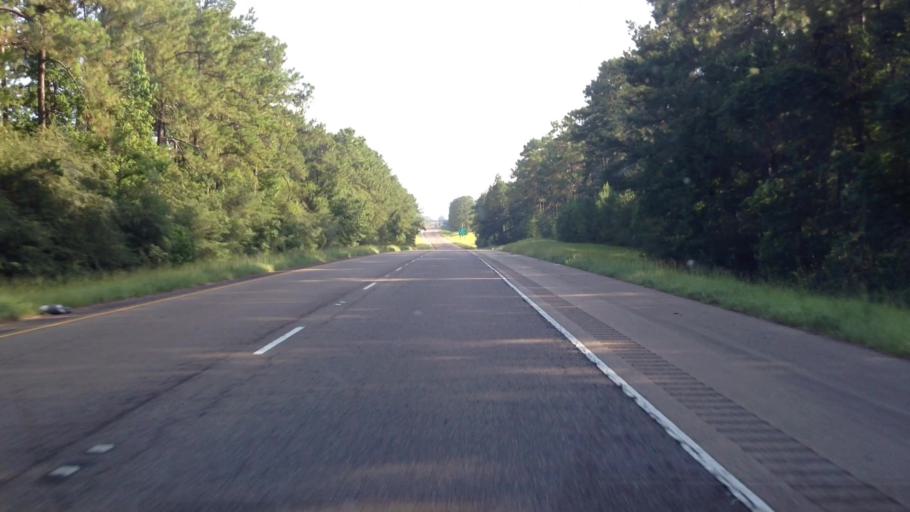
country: US
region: Louisiana
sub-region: Tangipahoa Parish
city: Roseland
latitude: 30.8097
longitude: -90.5327
